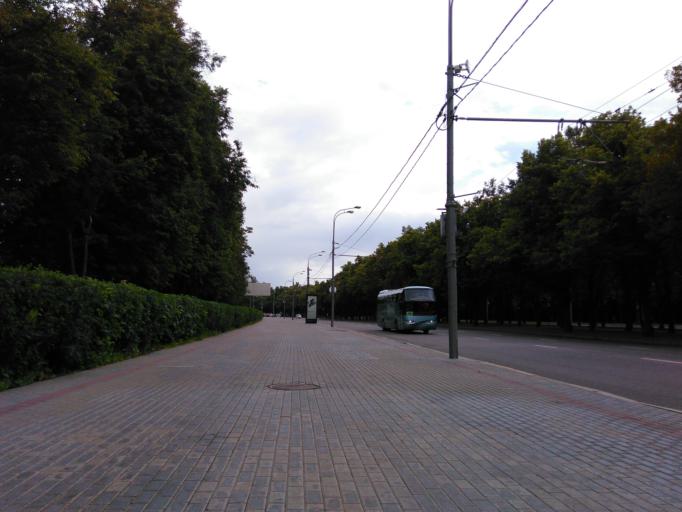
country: RU
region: Moscow
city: Vorob'yovo
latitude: 55.7129
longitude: 37.5378
